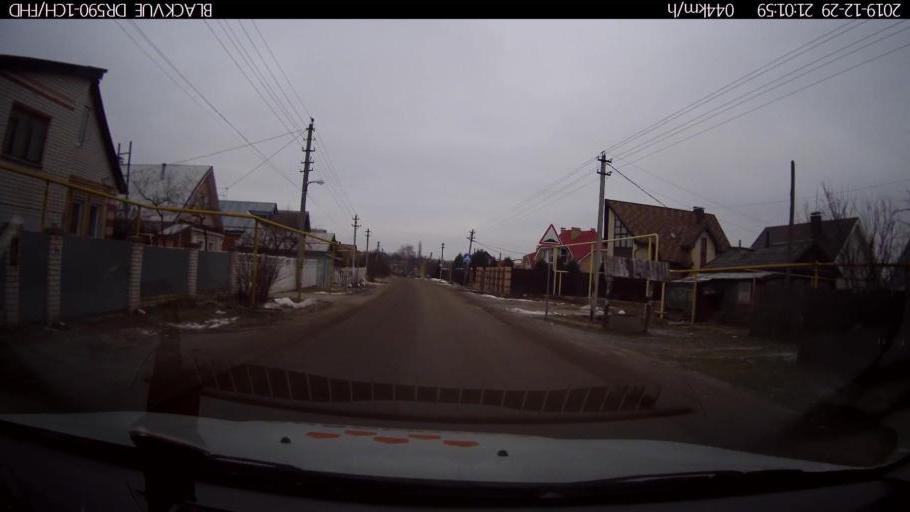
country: RU
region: Nizjnij Novgorod
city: Afonino
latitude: 56.1887
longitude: 43.9957
